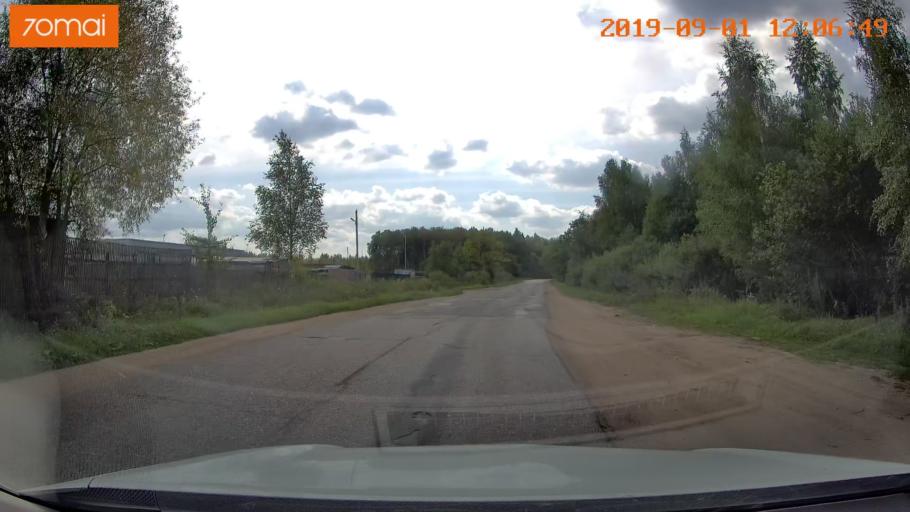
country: RU
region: Kaluga
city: Maloyaroslavets
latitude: 54.9857
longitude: 36.4715
